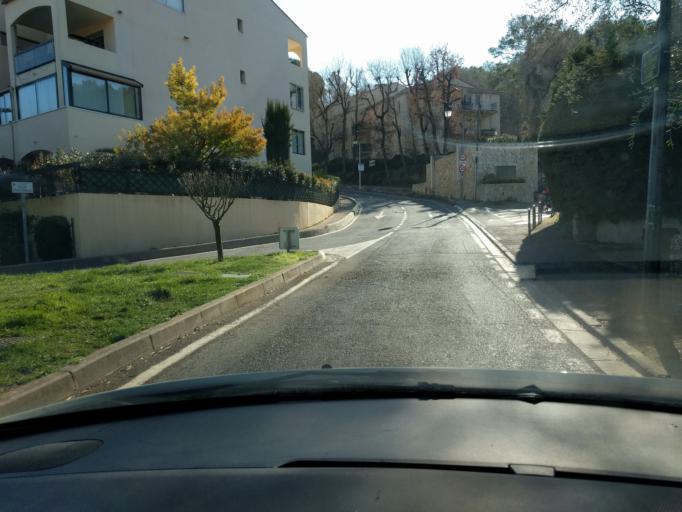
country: FR
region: Provence-Alpes-Cote d'Azur
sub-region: Departement des Alpes-Maritimes
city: Mougins
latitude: 43.6031
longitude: 6.9907
